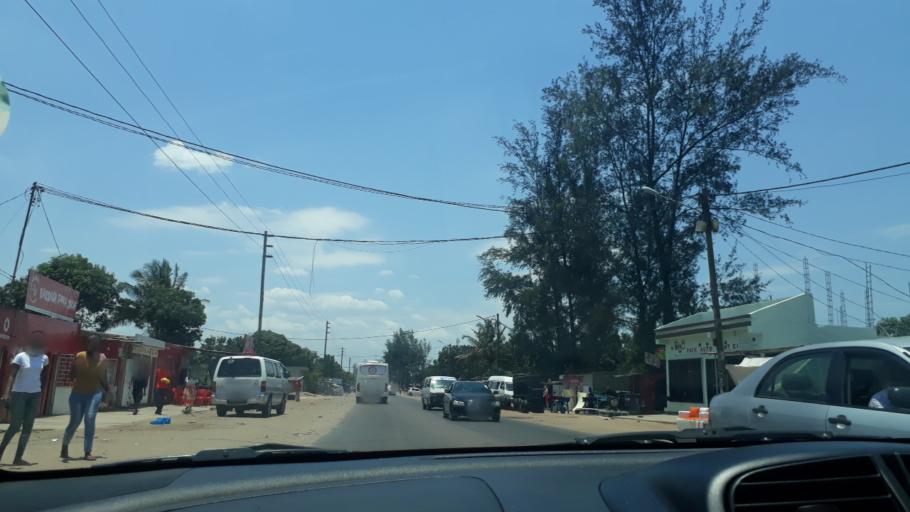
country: MZ
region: Maputo City
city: Maputo
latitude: -25.8957
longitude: 32.6008
